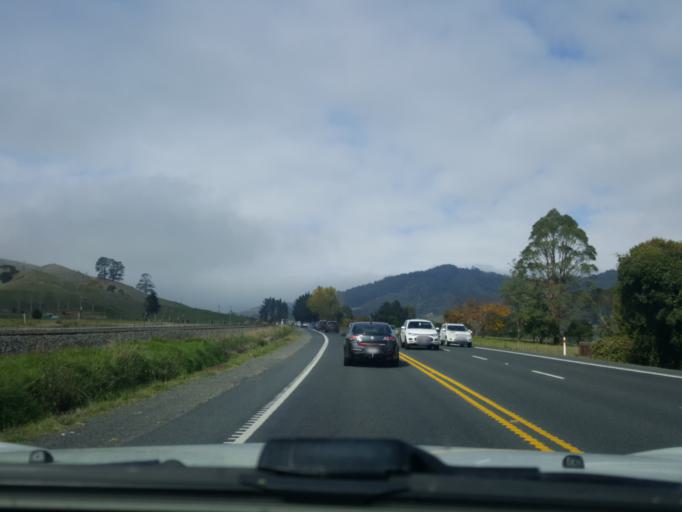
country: NZ
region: Waikato
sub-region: Waikato District
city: Ngaruawahia
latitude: -37.5933
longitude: 175.1600
